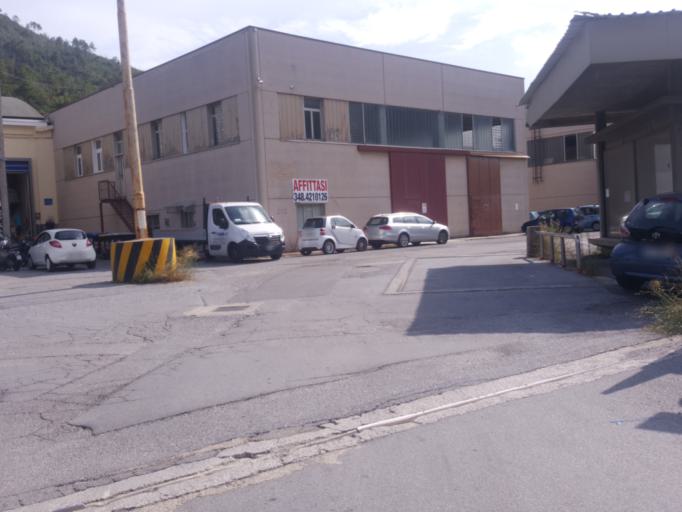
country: IT
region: Liguria
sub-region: Provincia di Savona
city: Valle di Vado
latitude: 44.2599
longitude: 8.4102
